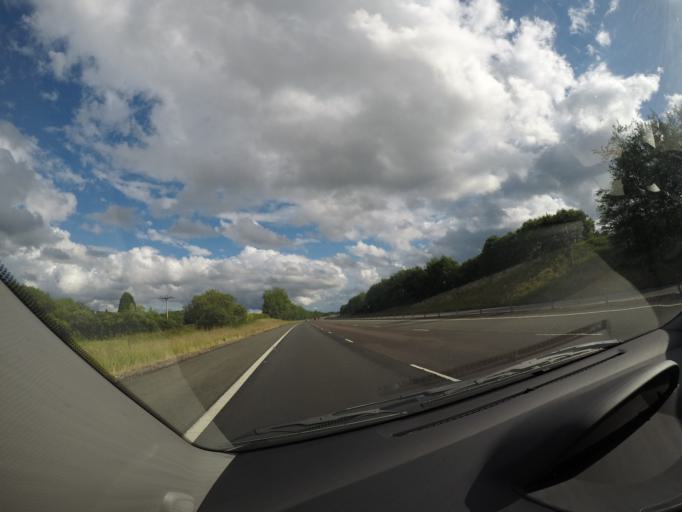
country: GB
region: Scotland
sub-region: Dumfries and Galloway
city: Moffat
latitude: 55.2537
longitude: -3.4108
